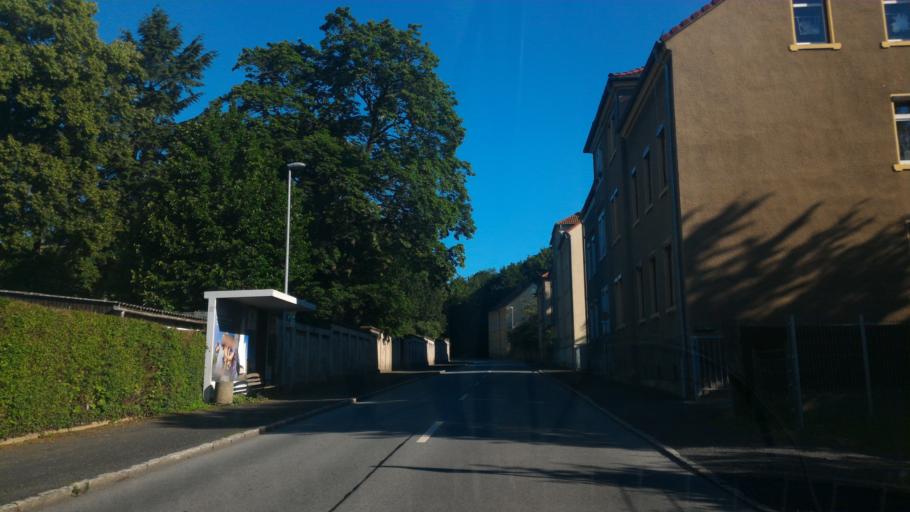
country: DE
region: Saxony
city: Zittau
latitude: 50.8949
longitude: 14.8207
